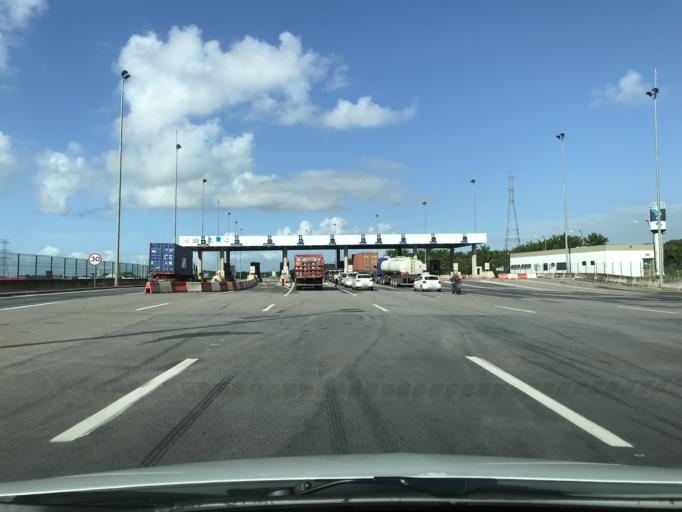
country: BR
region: Pernambuco
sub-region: Cabo De Santo Agostinho
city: Cabo
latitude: -8.2735
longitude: -34.9986
